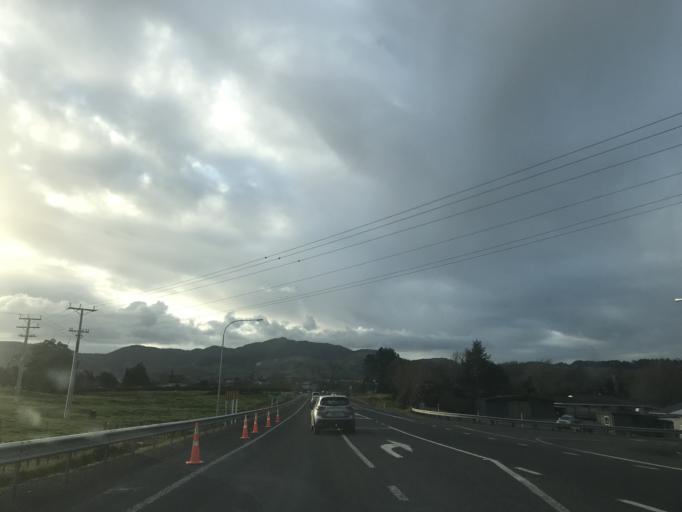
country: NZ
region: Waikato
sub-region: Hauraki District
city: Waihi
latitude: -37.4054
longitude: 175.8579
